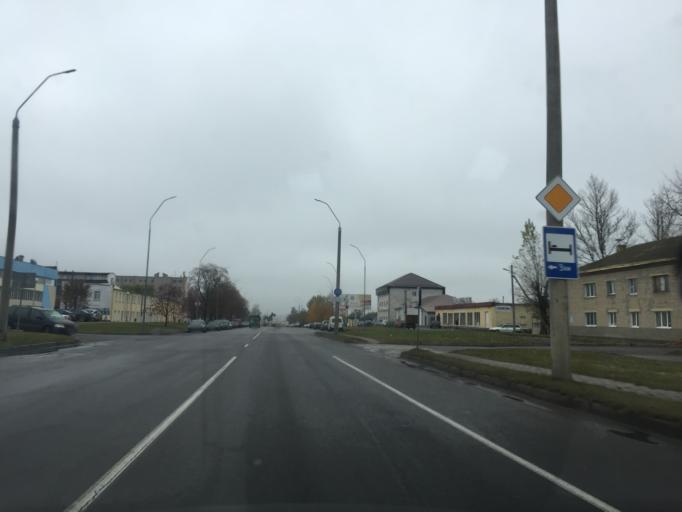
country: BY
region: Mogilev
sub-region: Mahilyowski Rayon
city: Veyno
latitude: 53.8605
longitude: 30.3585
